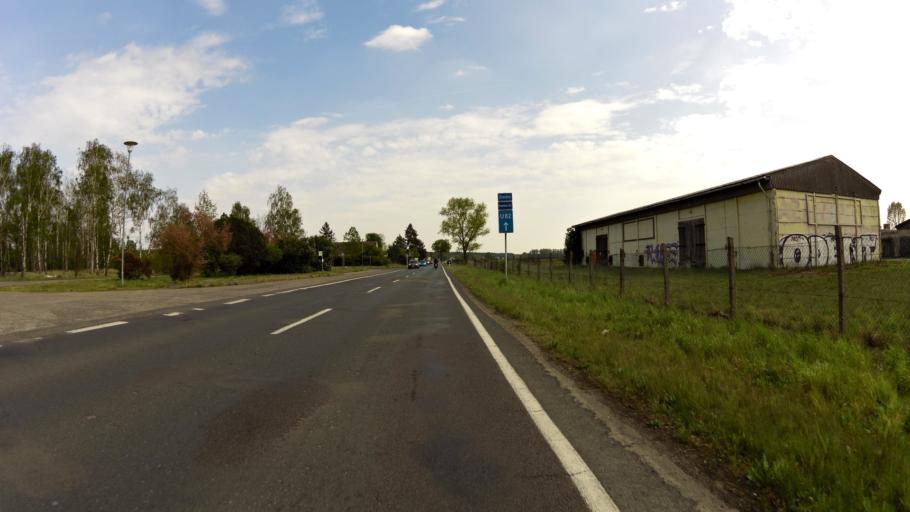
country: DE
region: Brandenburg
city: Spreenhagen
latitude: 52.3408
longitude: 13.8870
